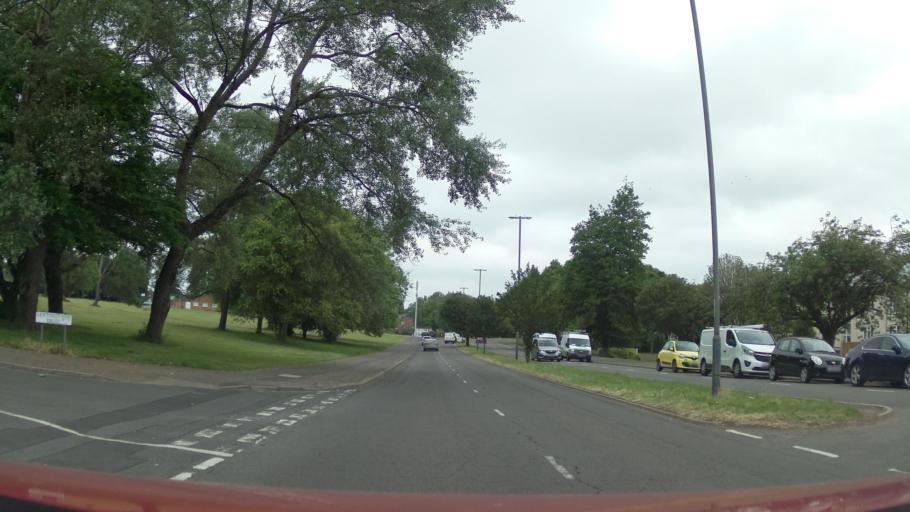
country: GB
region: England
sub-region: Derby
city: Derby
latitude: 52.9250
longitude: -1.5194
